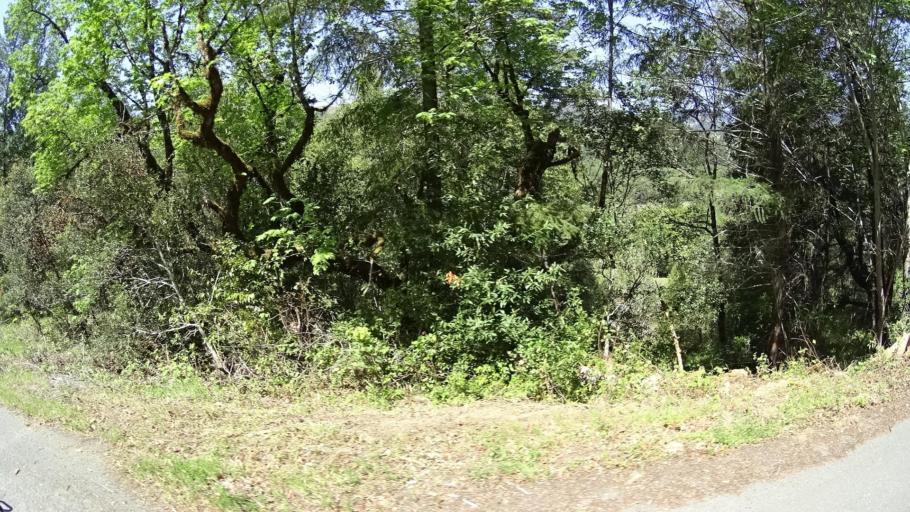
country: US
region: California
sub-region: Humboldt County
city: Redway
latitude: 40.2327
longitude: -123.6422
